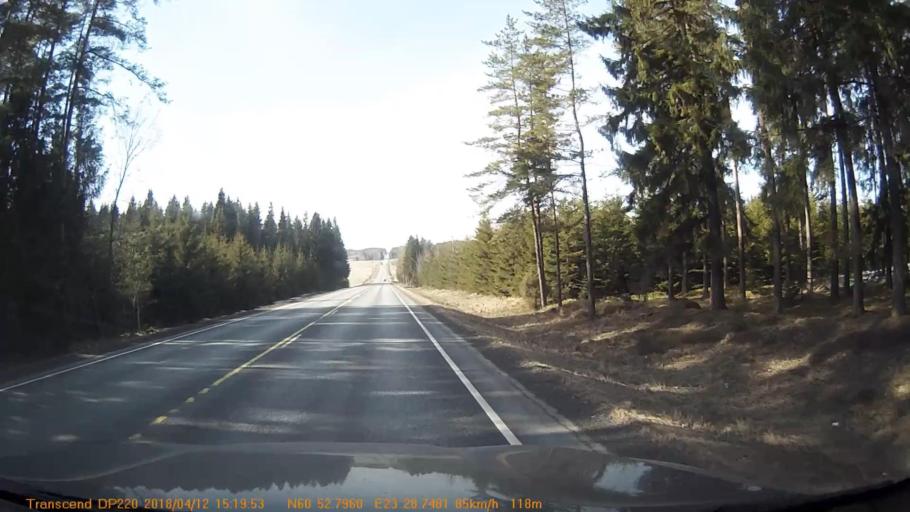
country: FI
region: Haeme
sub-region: Forssa
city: Jokioinen
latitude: 60.8804
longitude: 23.4781
